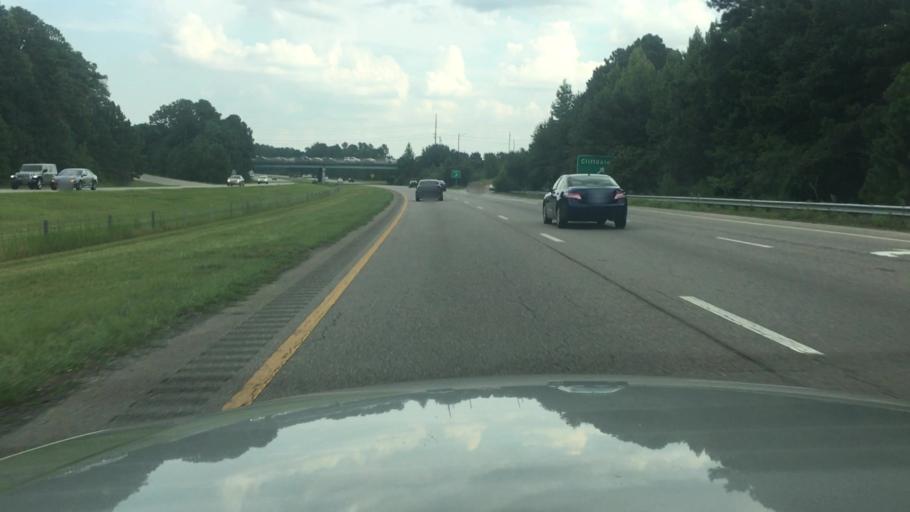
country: US
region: North Carolina
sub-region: Cumberland County
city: Fayetteville
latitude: 35.0620
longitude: -78.9553
